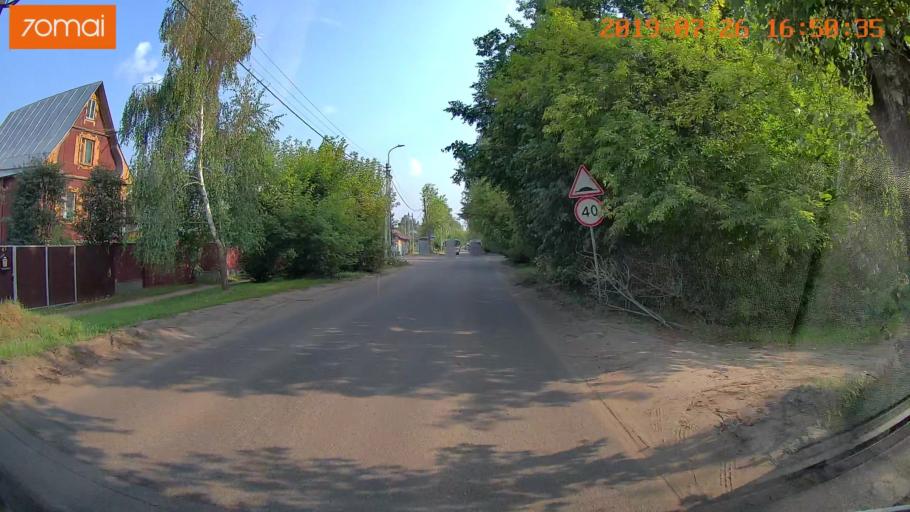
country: RU
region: Ivanovo
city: Bogorodskoye
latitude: 57.0230
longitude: 41.0207
